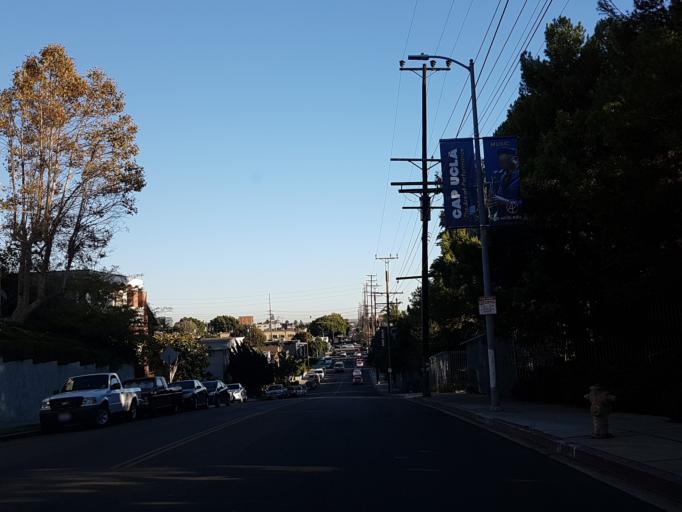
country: US
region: California
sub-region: Los Angeles County
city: Westwood, Los Angeles
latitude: 34.0462
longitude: -118.4582
